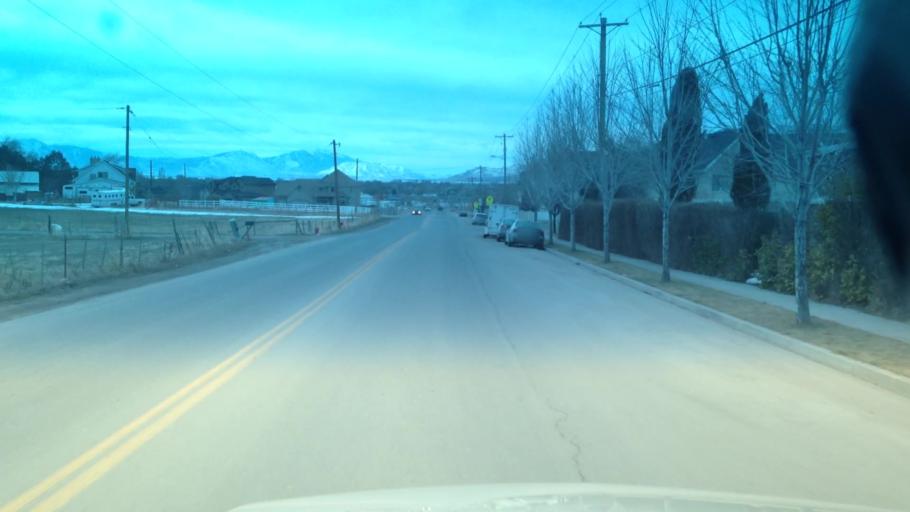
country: US
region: Utah
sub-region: Utah County
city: Lehi
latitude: 40.4249
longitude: -111.8689
